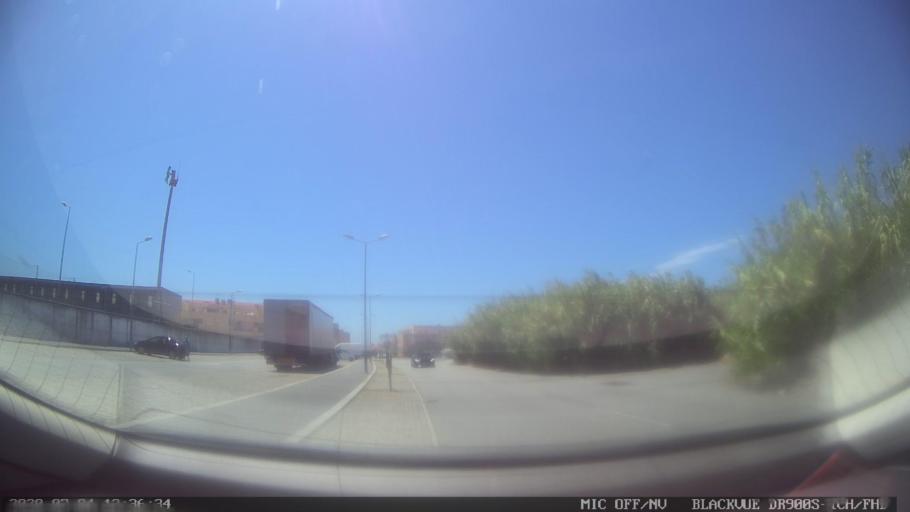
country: PT
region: Porto
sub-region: Matosinhos
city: Lavra
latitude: 41.2545
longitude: -8.7195
